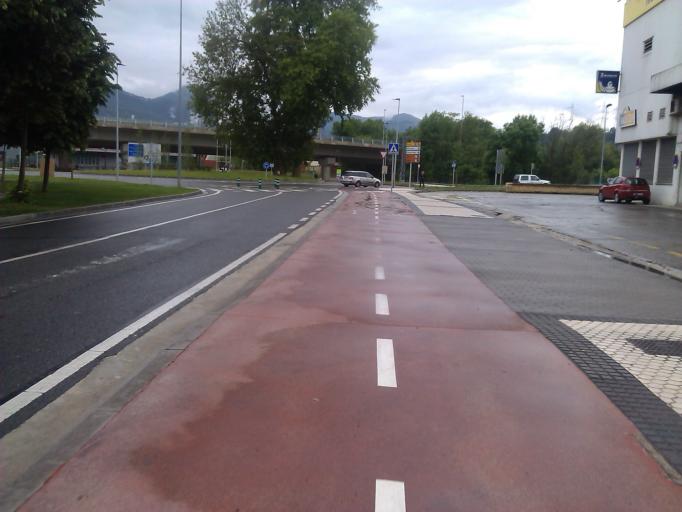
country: ES
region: Basque Country
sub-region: Provincia de Guipuzcoa
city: Hernani
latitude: 43.2666
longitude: -1.9689
